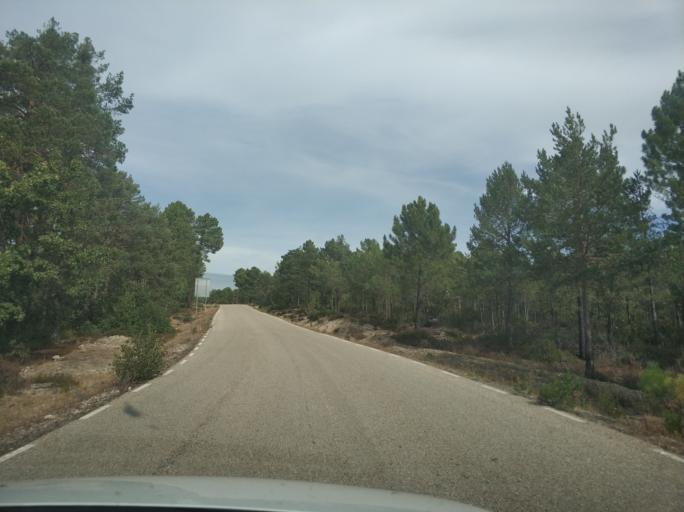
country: ES
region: Castille and Leon
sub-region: Provincia de Soria
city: Duruelo de la Sierra
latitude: 41.8813
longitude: -2.9362
